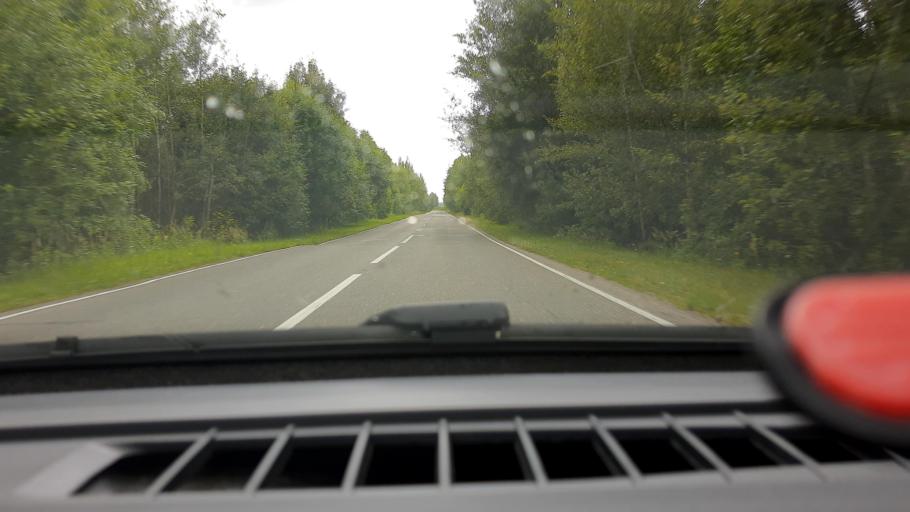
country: RU
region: Nizjnij Novgorod
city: Neklyudovo
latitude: 56.5078
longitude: 43.9670
